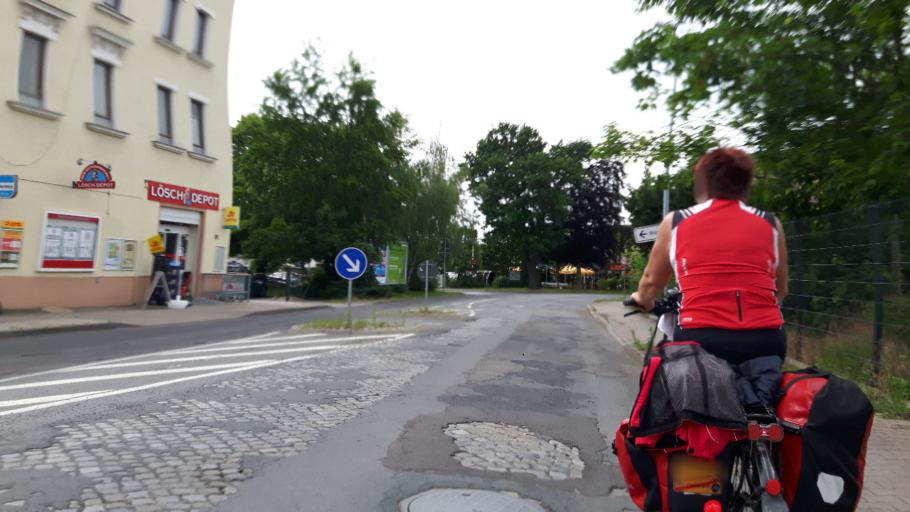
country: DE
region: Saxony
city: Rackwitz
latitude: 51.3941
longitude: 12.3390
